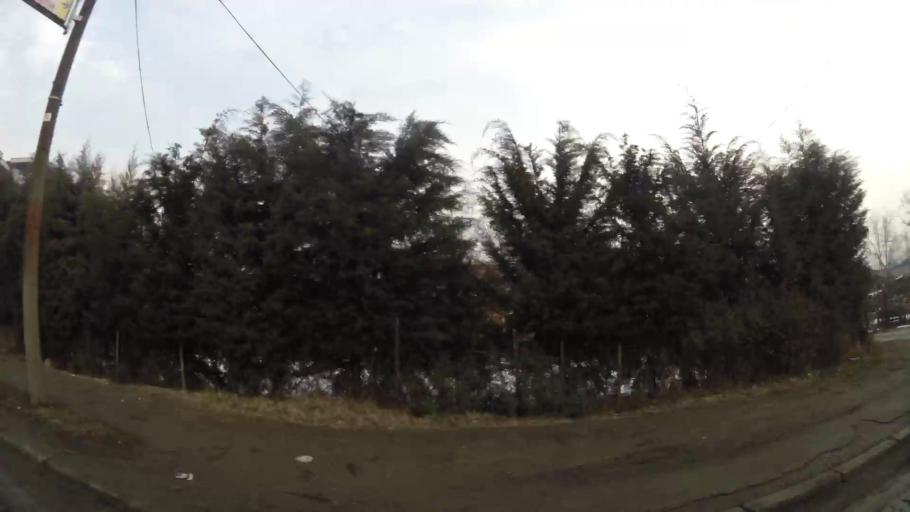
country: MK
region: Kisela Voda
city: Kisela Voda
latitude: 41.9927
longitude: 21.5075
